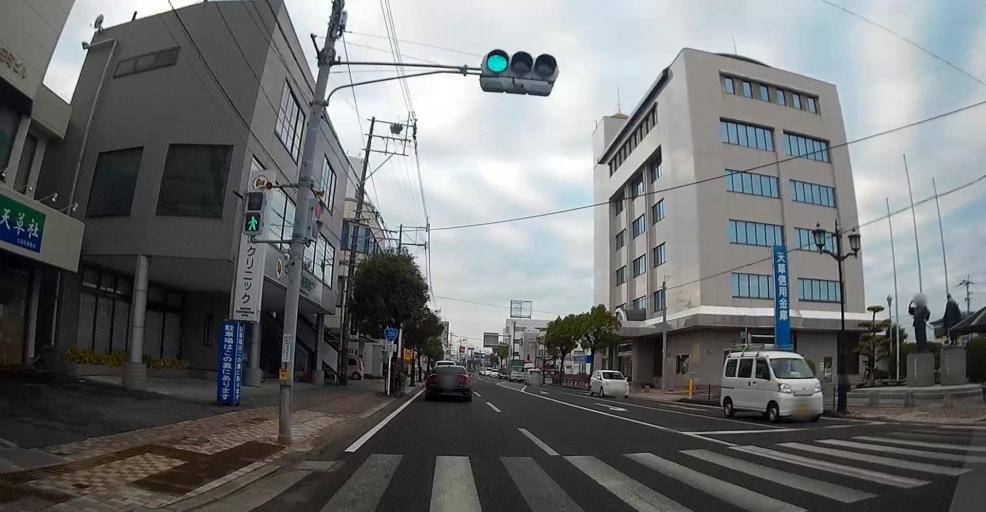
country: JP
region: Kumamoto
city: Hondo
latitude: 32.4510
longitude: 130.1976
